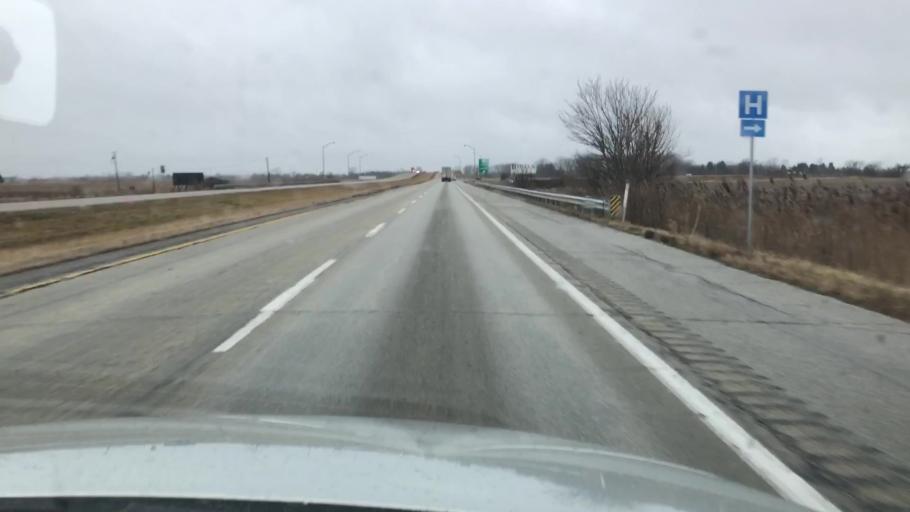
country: US
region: Indiana
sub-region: Starke County
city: Knox
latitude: 41.3940
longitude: -86.6117
